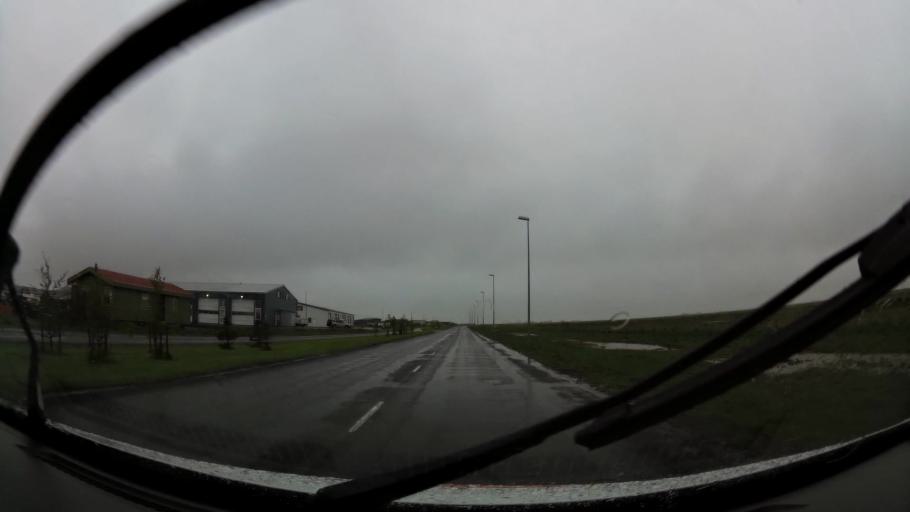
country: IS
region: South
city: Selfoss
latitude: 63.9276
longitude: -21.0184
